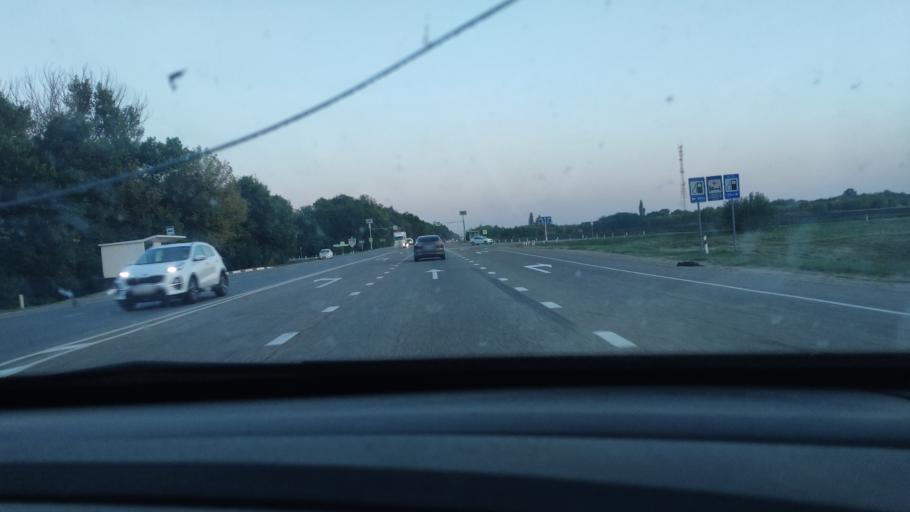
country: RU
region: Krasnodarskiy
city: Medvedovskaya
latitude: 45.4546
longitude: 38.9892
